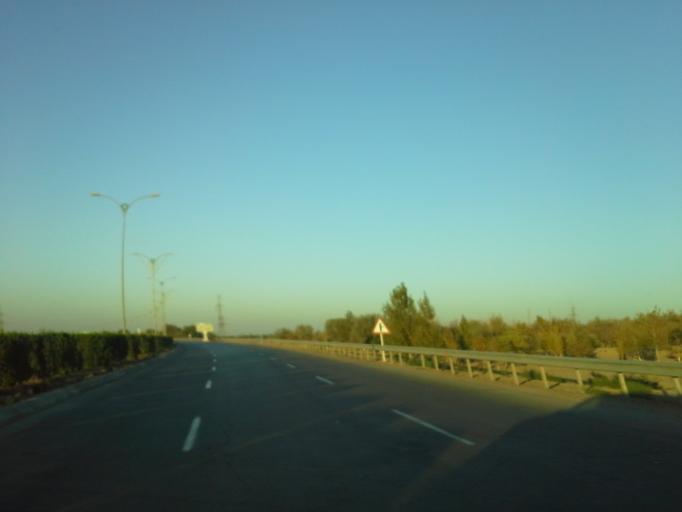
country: TM
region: Dasoguz
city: Dasoguz
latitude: 41.7917
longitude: 59.8836
